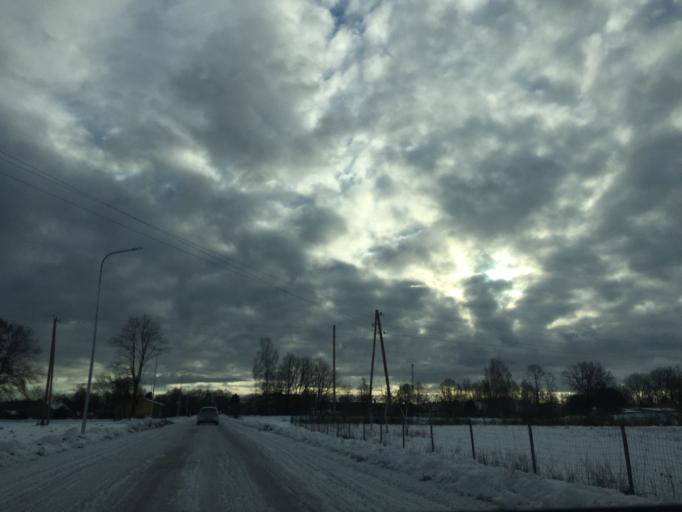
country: LV
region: Lielvarde
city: Lielvarde
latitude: 56.6357
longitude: 24.7505
